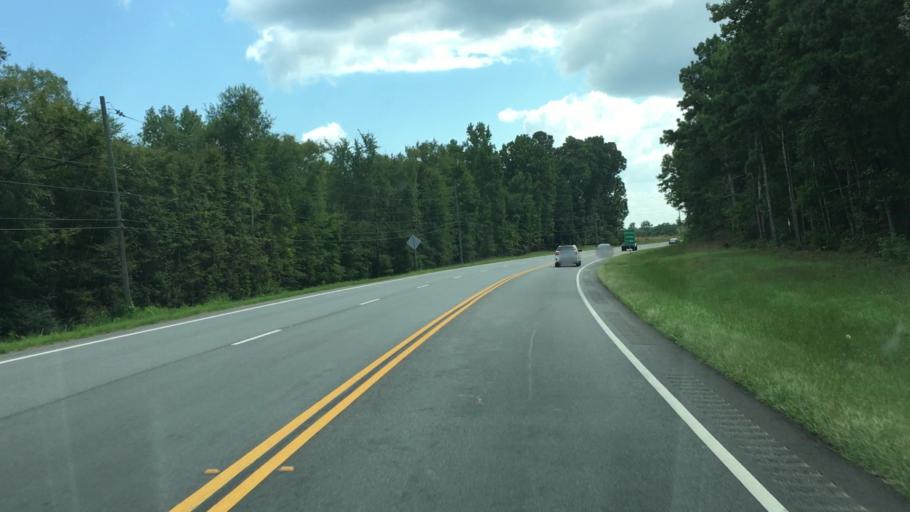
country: US
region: Georgia
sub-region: Putnam County
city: Jefferson
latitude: 33.4259
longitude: -83.3702
